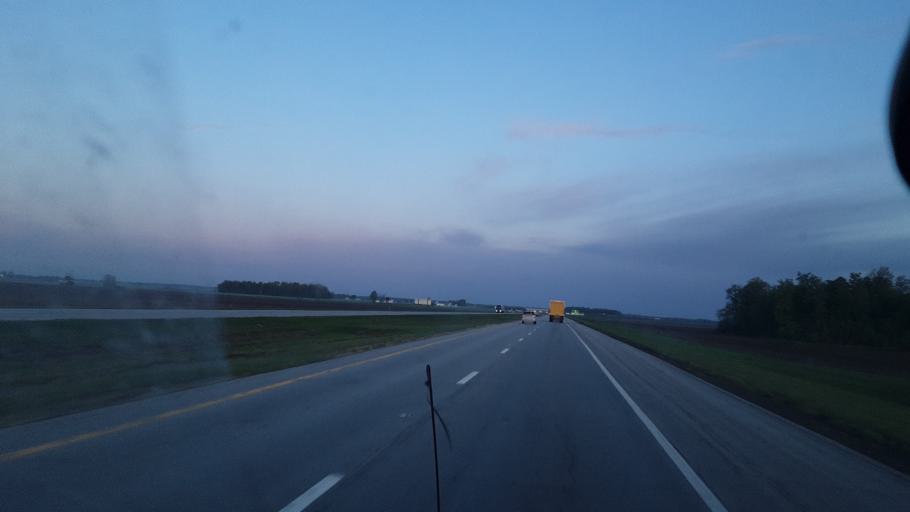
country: US
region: Ohio
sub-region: Hardin County
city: Forest
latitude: 40.8270
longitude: -83.4986
